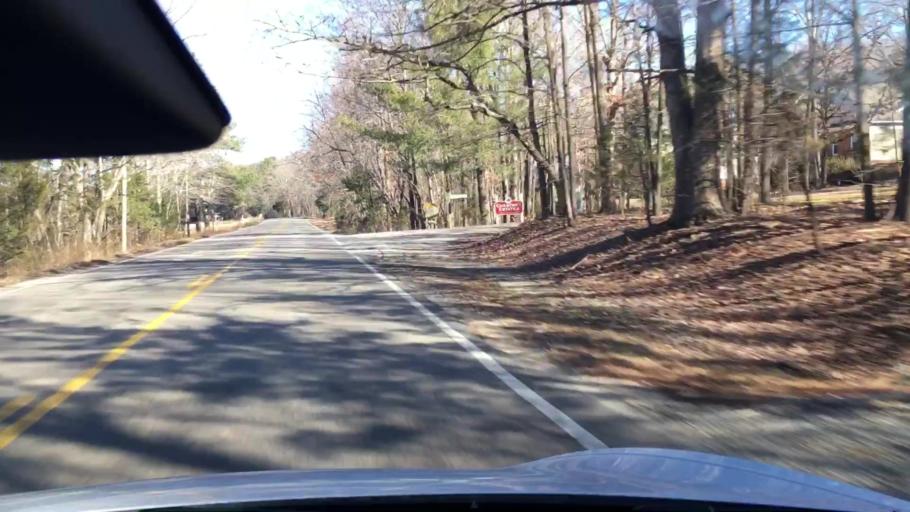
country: US
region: Virginia
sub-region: Powhatan County
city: Powhatan
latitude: 37.5333
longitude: -77.7998
